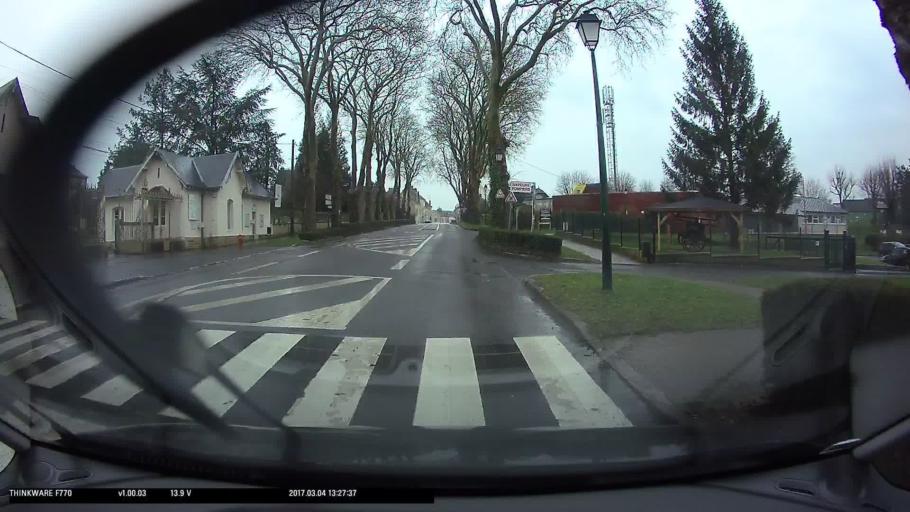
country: FR
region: Ile-de-France
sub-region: Departement du Val-d'Oise
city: Marines
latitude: 49.1468
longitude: 1.9748
